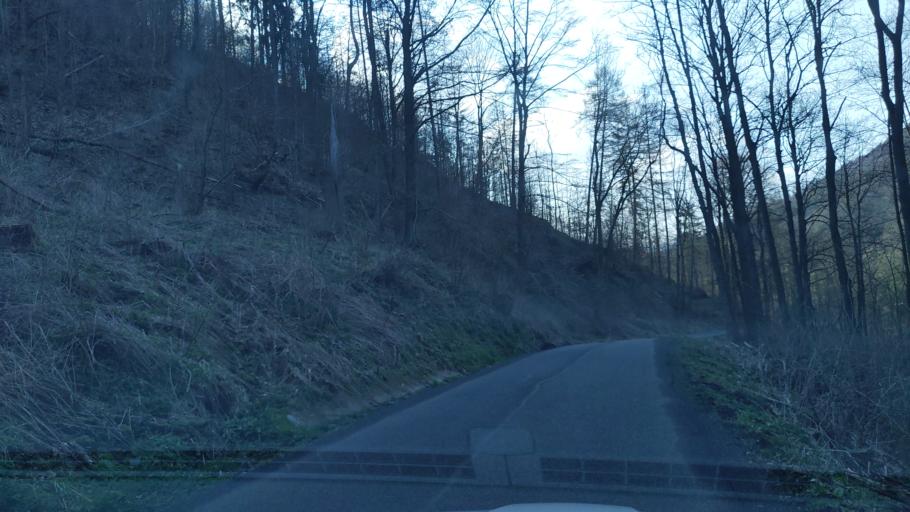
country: CZ
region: Ustecky
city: Povrly
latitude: 50.7026
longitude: 14.2324
